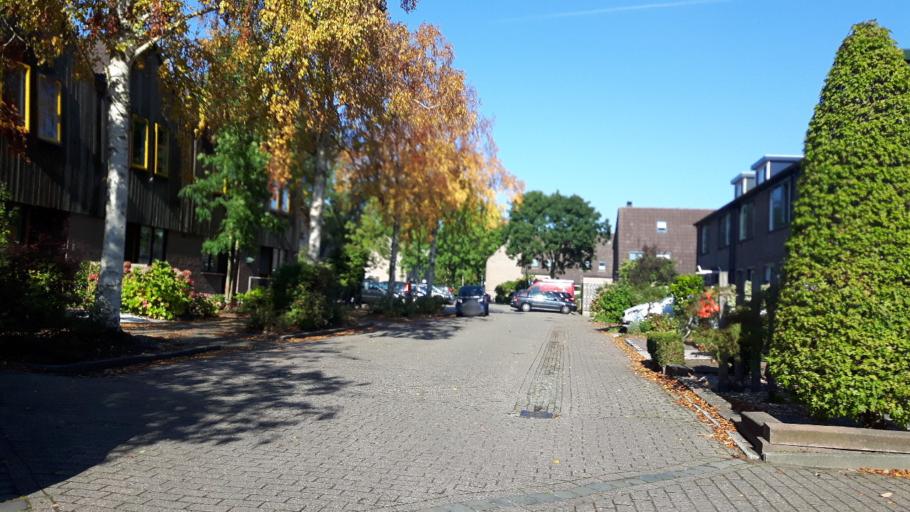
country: NL
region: South Holland
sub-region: Molenwaard
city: Liesveld
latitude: 51.9363
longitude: 4.7921
